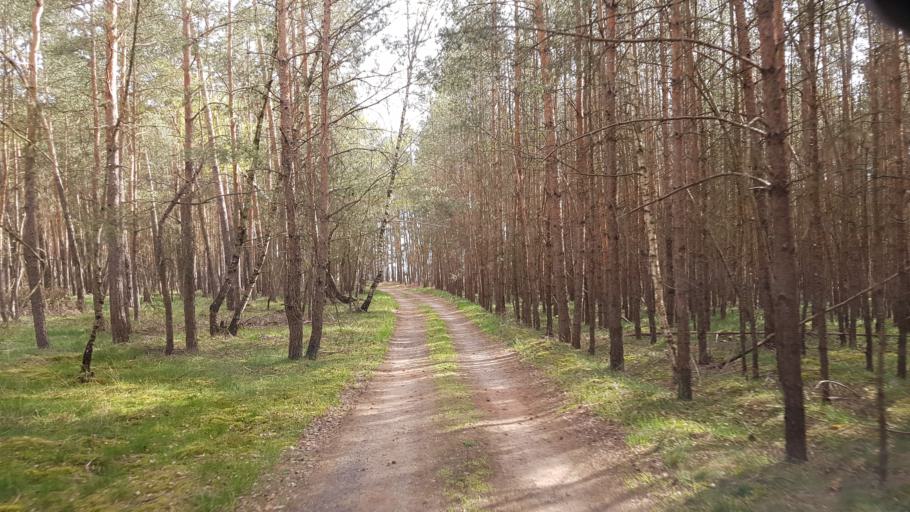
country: DE
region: Brandenburg
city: Bad Liebenwerda
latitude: 51.5439
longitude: 13.3400
